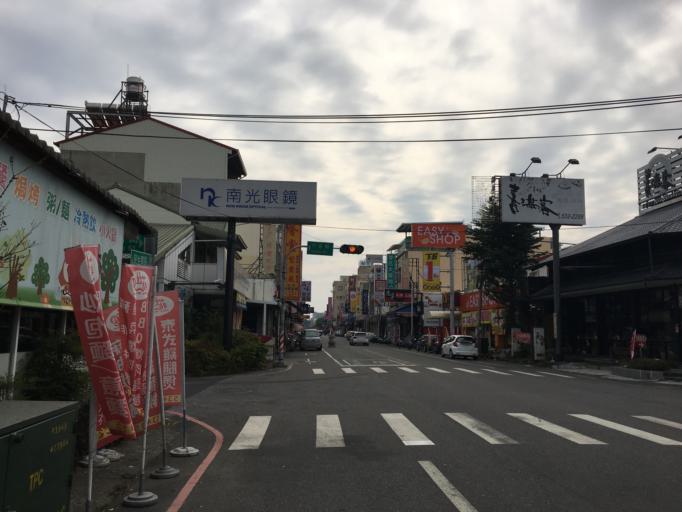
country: TW
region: Taiwan
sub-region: Yunlin
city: Douliu
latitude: 23.7061
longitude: 120.5370
